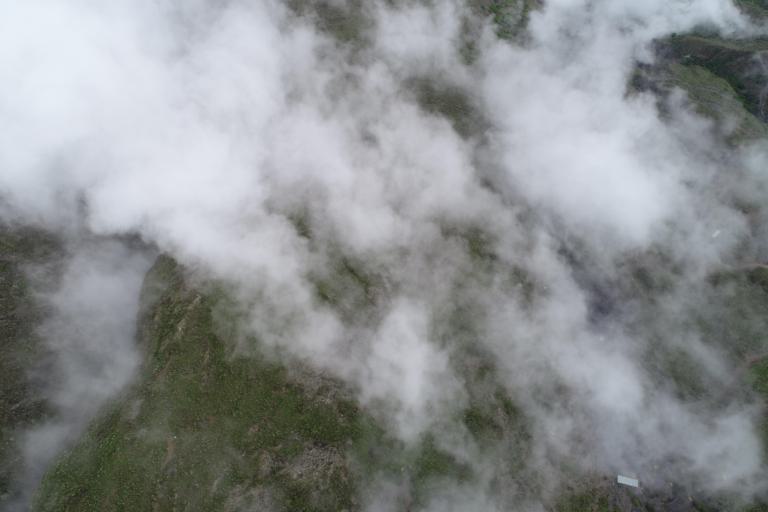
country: BO
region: La Paz
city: Sorata
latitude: -15.5195
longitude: -68.6656
